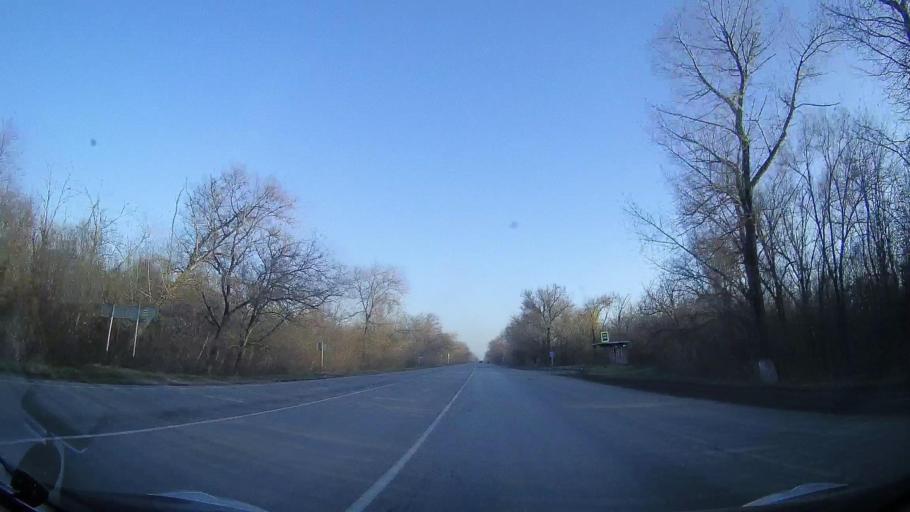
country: RU
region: Rostov
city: Bataysk
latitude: 47.0480
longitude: 39.8428
